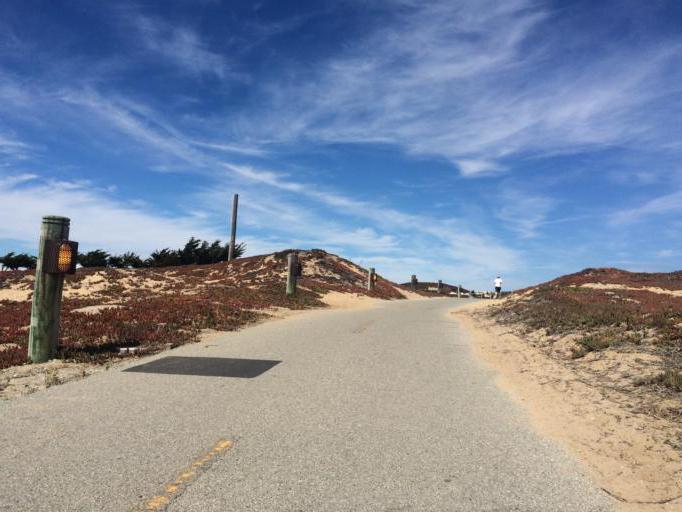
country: US
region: California
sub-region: Monterey County
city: Seaside
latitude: 36.6216
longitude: -121.8468
